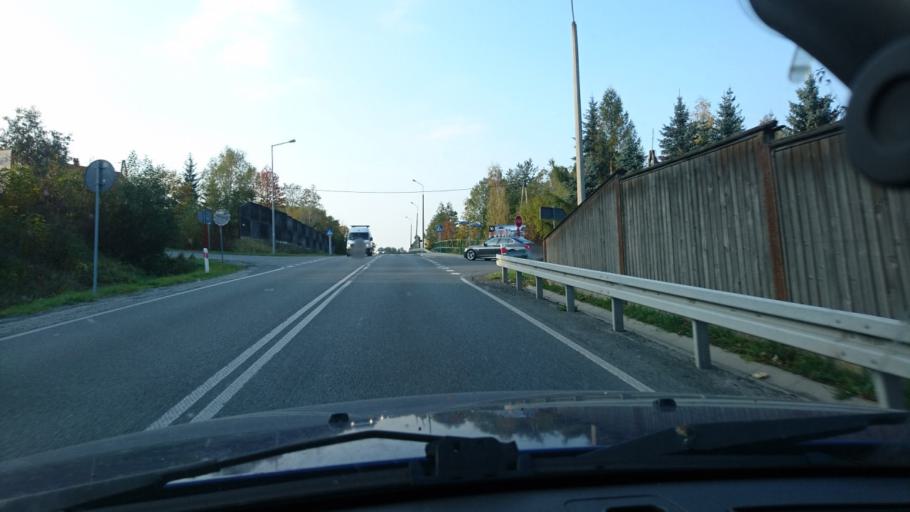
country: PL
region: Silesian Voivodeship
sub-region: Powiat cieszynski
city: Ustron
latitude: 49.7133
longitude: 18.8074
